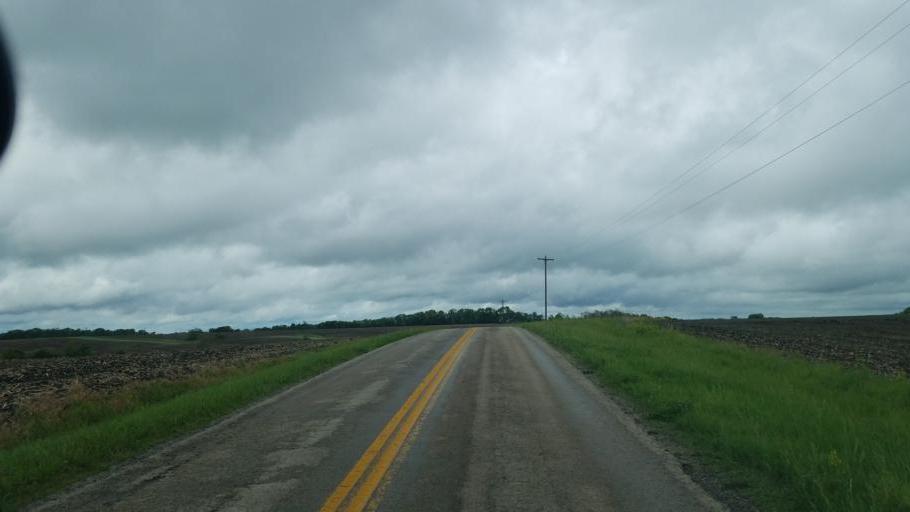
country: US
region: Missouri
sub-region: Mercer County
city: Princeton
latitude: 40.4677
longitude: -93.6914
